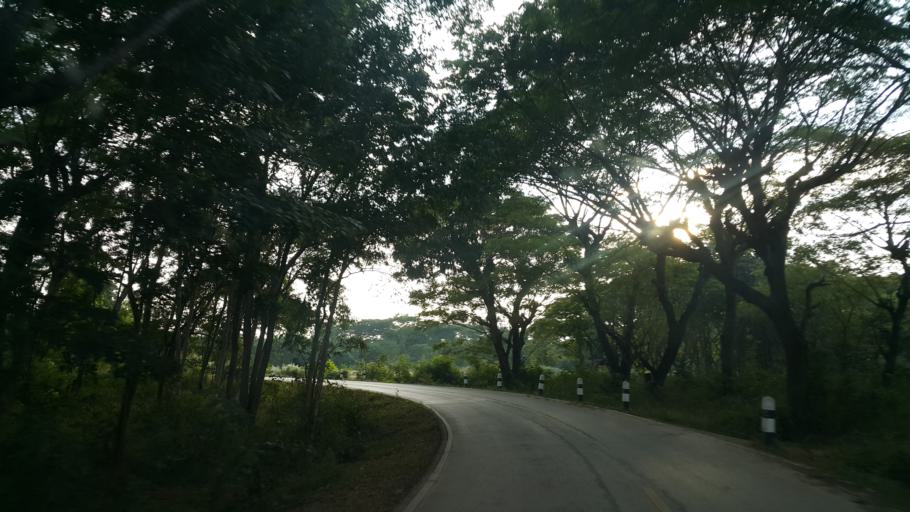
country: TH
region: Lampang
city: Sop Prap
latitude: 17.9262
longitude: 99.3337
